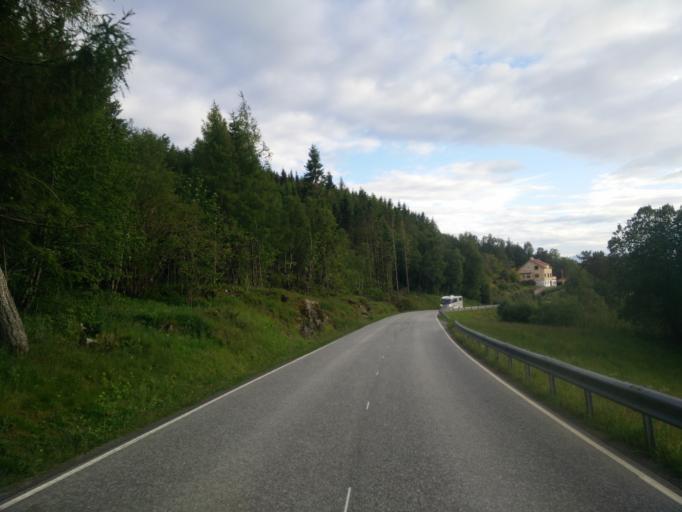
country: NO
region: More og Romsdal
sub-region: Kristiansund
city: Rensvik
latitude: 63.0207
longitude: 8.0134
